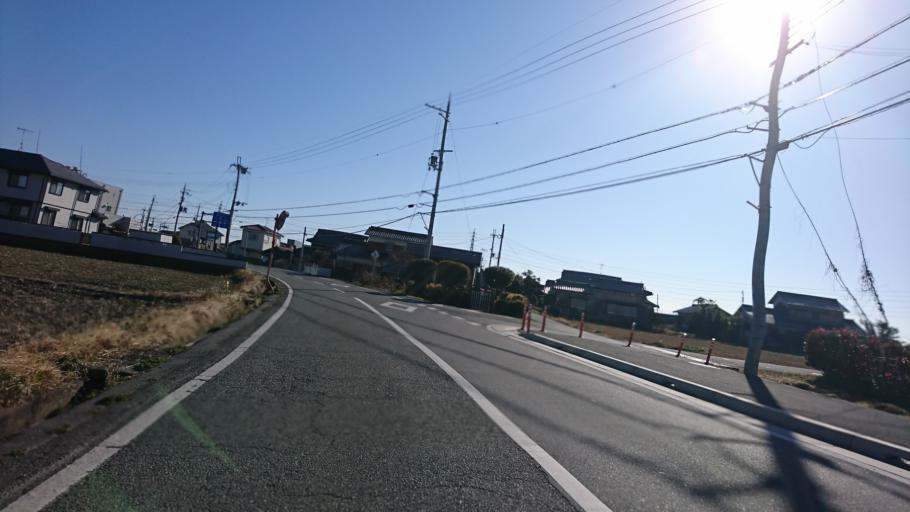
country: JP
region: Hyogo
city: Miki
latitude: 34.7469
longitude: 134.9340
